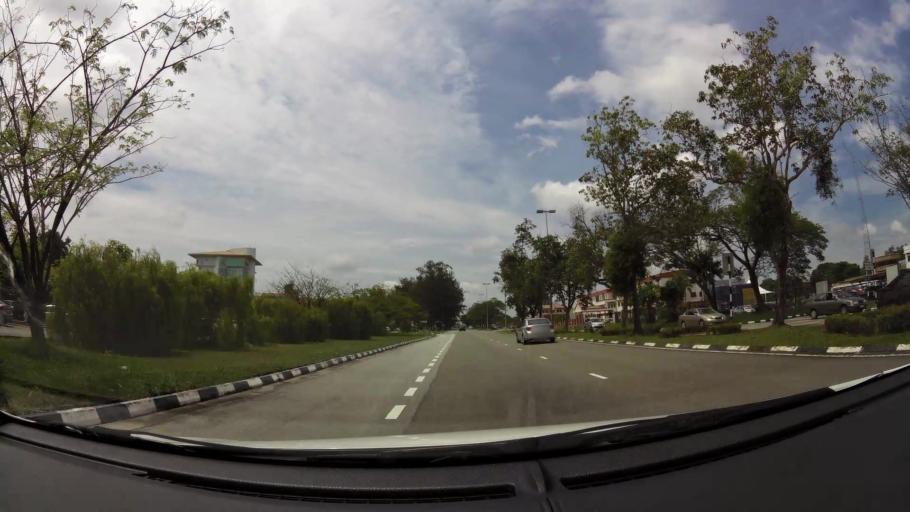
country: BN
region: Brunei and Muara
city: Bandar Seri Begawan
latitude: 4.9236
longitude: 114.9307
